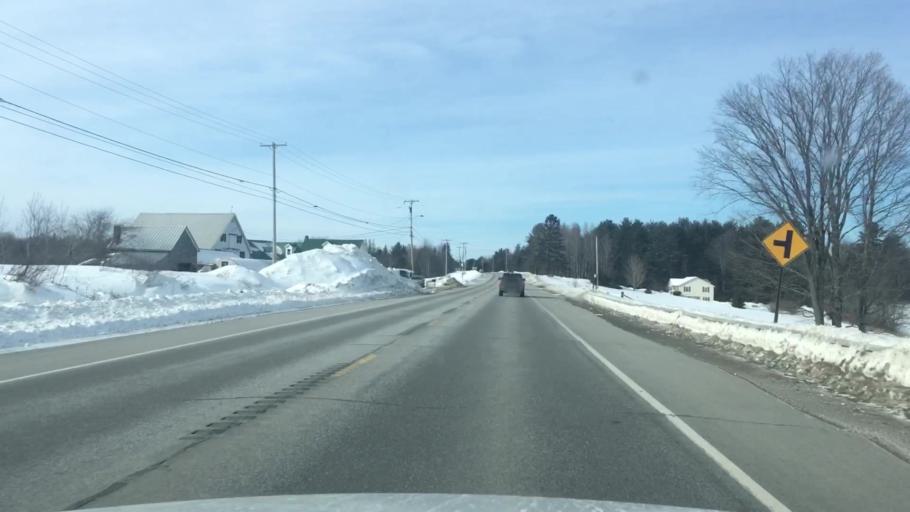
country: US
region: Maine
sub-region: Penobscot County
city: Kenduskeag
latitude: 44.9515
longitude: -68.9484
